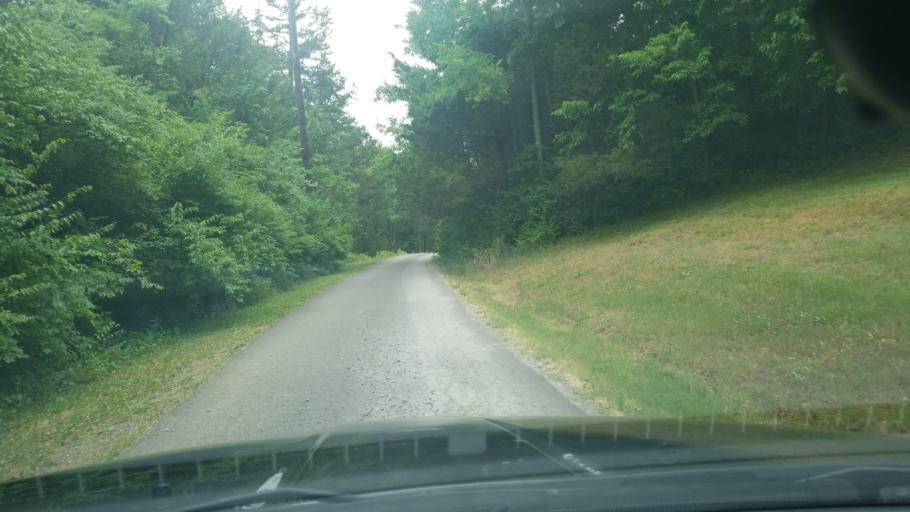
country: US
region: Tennessee
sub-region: Davidson County
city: Goodlettsville
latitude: 36.2571
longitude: -86.7524
